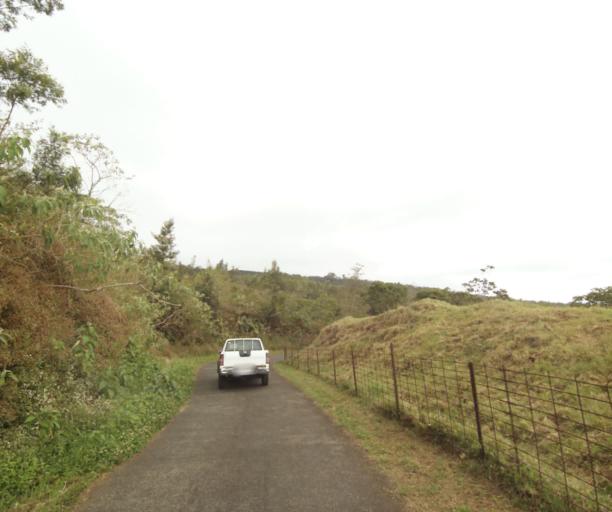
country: RE
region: Reunion
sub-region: Reunion
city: Saint-Paul
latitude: -21.0178
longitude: 55.3490
